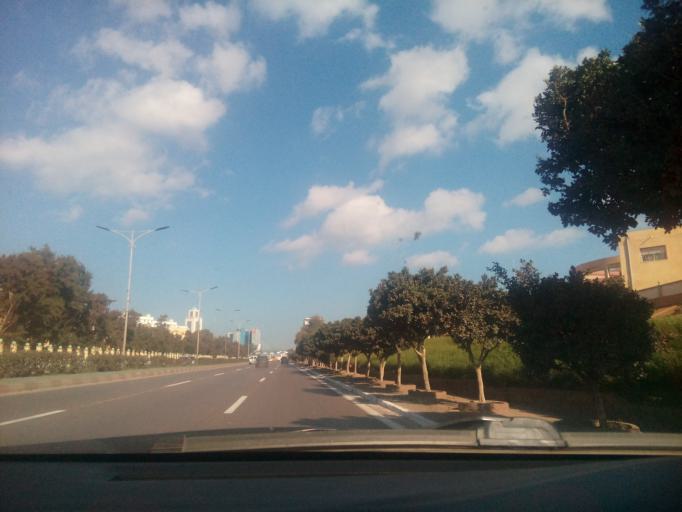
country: DZ
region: Oran
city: Oran
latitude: 35.6899
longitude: -0.6073
